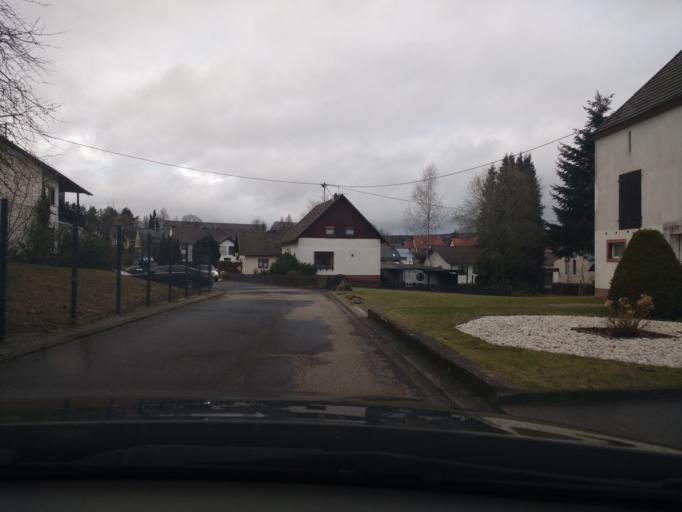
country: DE
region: Rheinland-Pfalz
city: Schillingen
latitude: 49.6356
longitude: 6.7873
